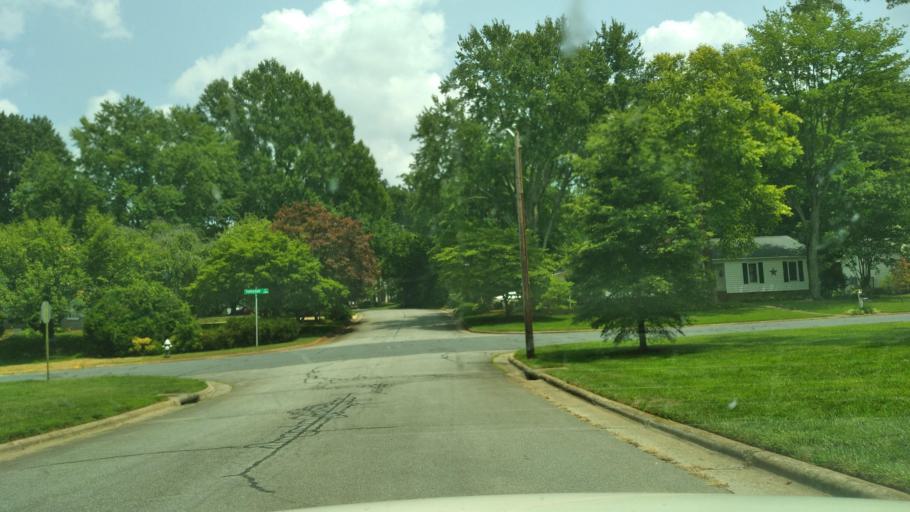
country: US
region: North Carolina
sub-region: Guilford County
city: Greensboro
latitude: 36.1220
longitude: -79.8517
